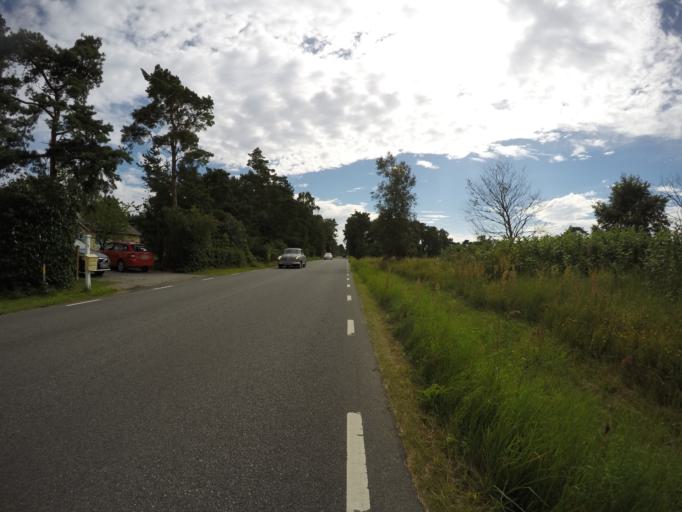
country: SE
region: Skane
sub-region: Simrishamns Kommun
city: Simrishamn
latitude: 55.4202
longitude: 14.2115
